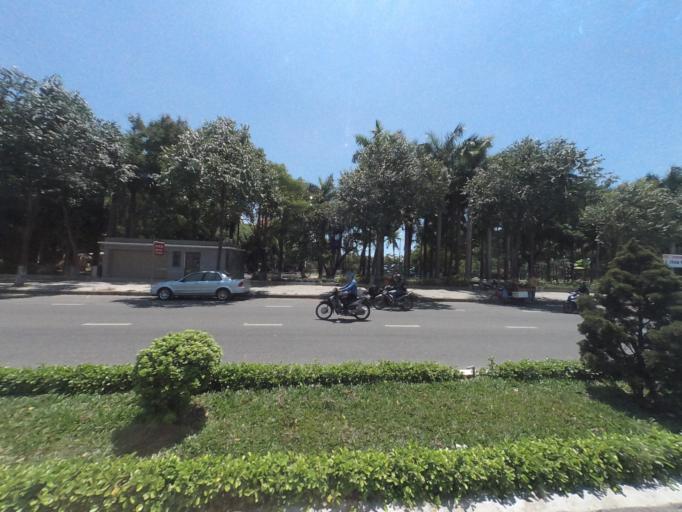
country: VN
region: Da Nang
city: Thanh Khe
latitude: 16.0646
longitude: 108.2031
